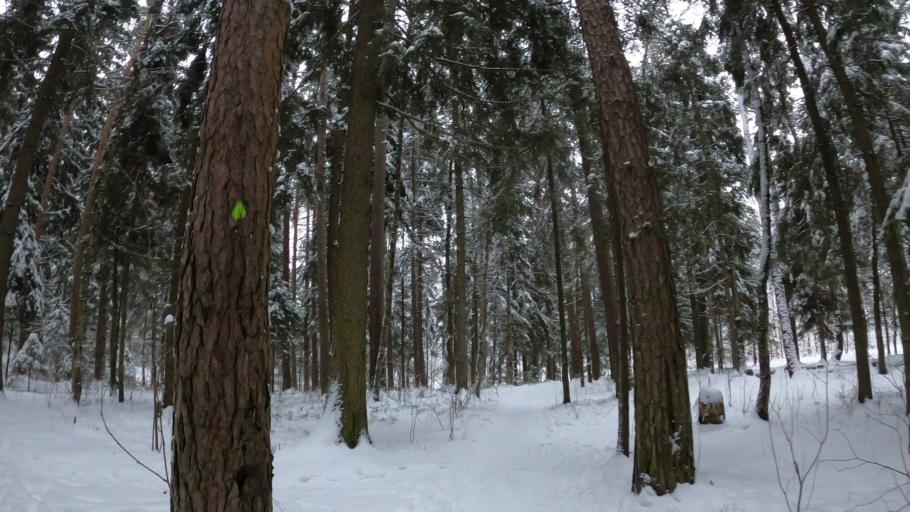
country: RU
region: Moskovskaya
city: Firsanovka
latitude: 55.9342
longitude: 37.2206
